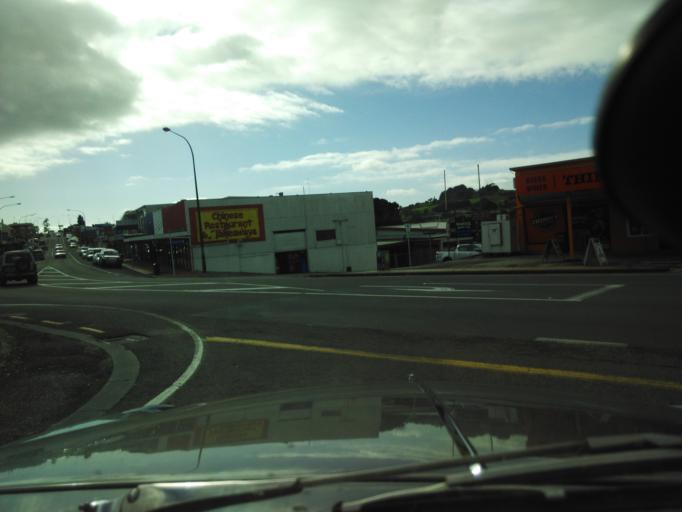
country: NZ
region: Auckland
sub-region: Auckland
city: Wellsford
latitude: -36.2961
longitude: 174.5232
